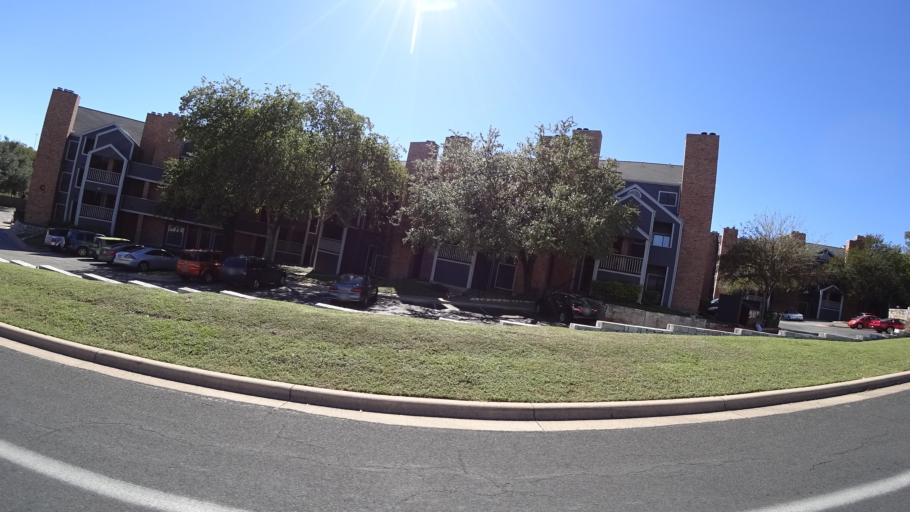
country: US
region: Texas
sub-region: Travis County
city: Rollingwood
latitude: 30.2303
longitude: -97.7767
